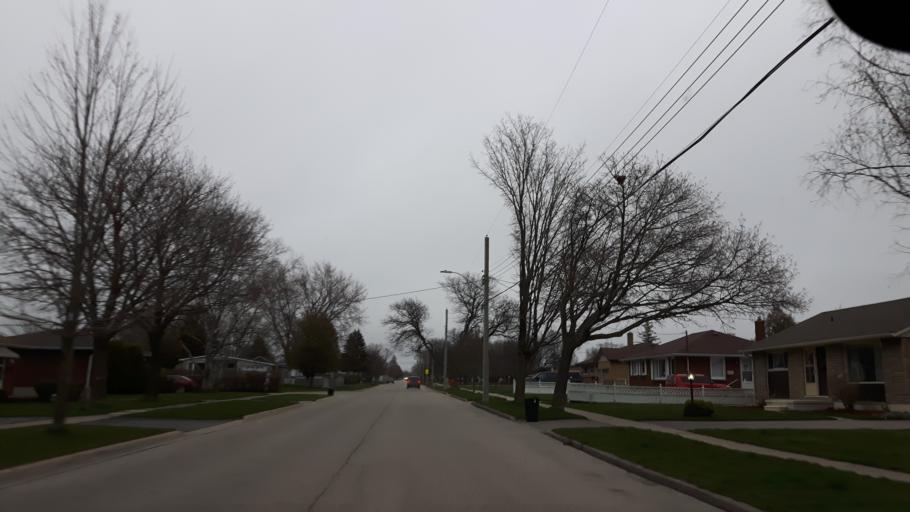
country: CA
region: Ontario
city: Goderich
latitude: 43.7353
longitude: -81.7200
